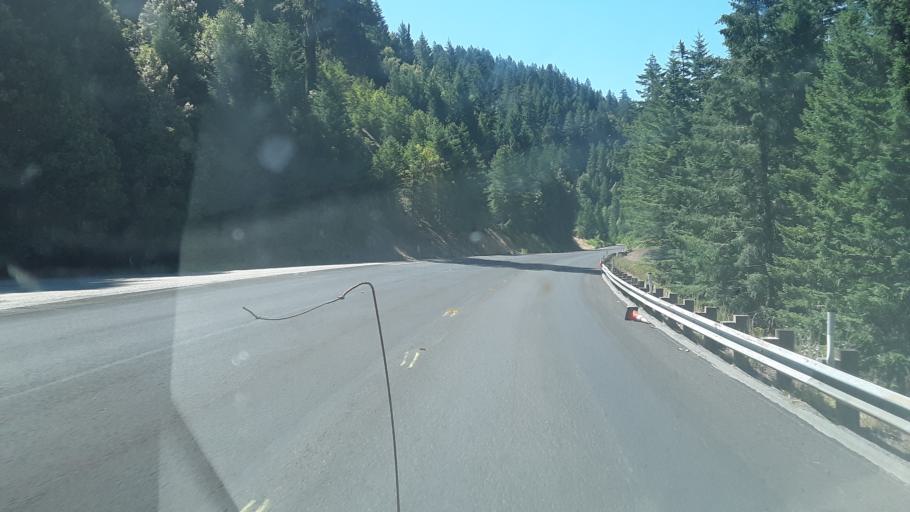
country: US
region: Oregon
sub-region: Josephine County
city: Cave Junction
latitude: 41.9550
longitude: -123.7433
